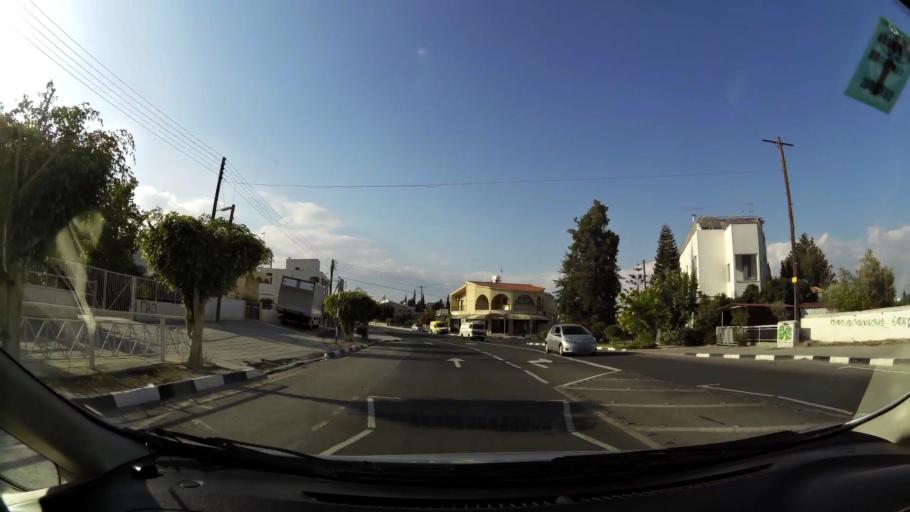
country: CY
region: Larnaka
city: Aradippou
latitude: 34.9443
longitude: 33.5968
